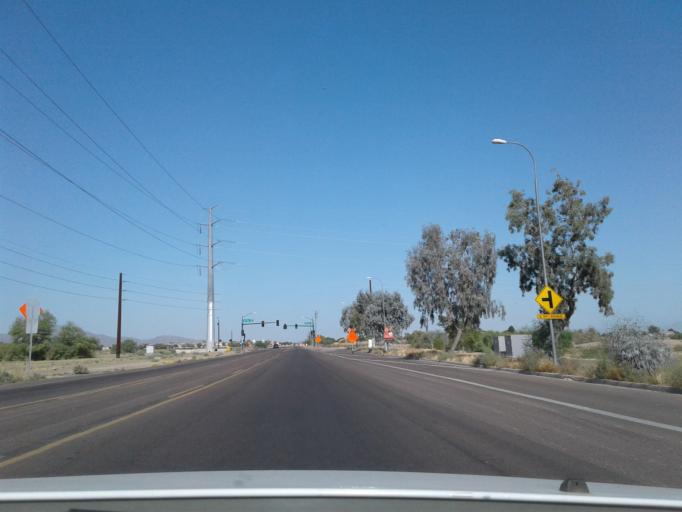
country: US
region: Arizona
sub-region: Maricopa County
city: Laveen
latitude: 33.3775
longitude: -112.1834
